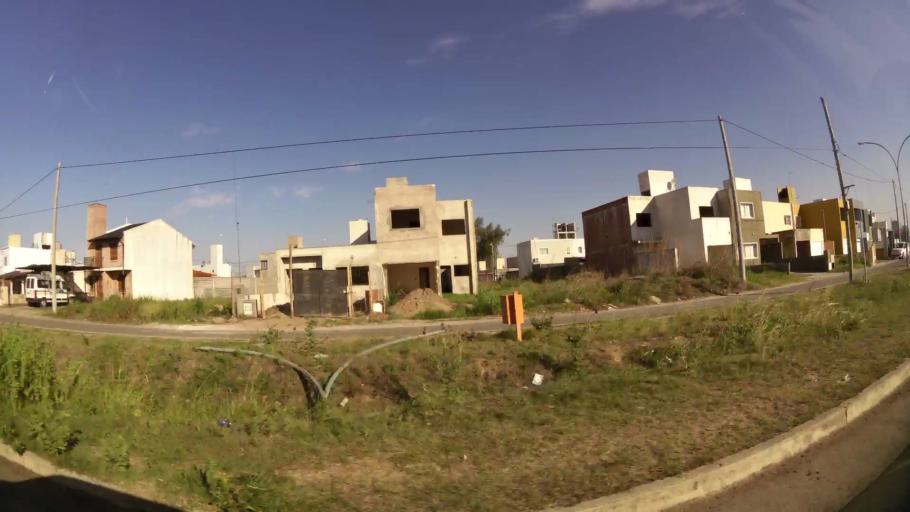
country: AR
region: Cordoba
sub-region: Departamento de Capital
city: Cordoba
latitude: -31.3551
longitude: -64.2250
